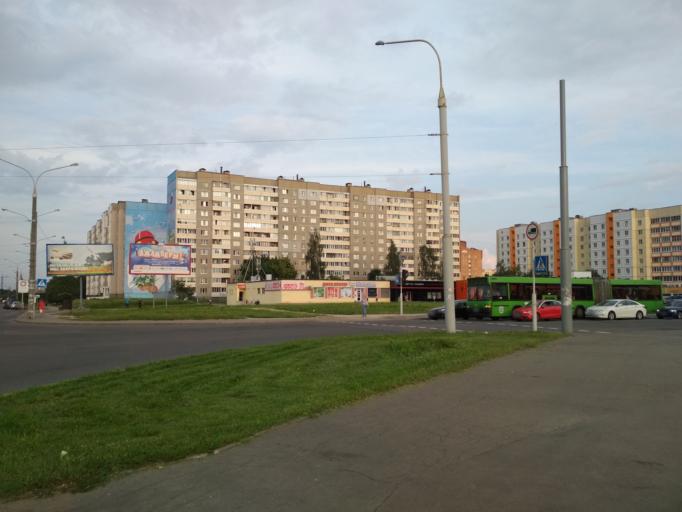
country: BY
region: Minsk
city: Minsk
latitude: 53.8855
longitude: 27.5509
